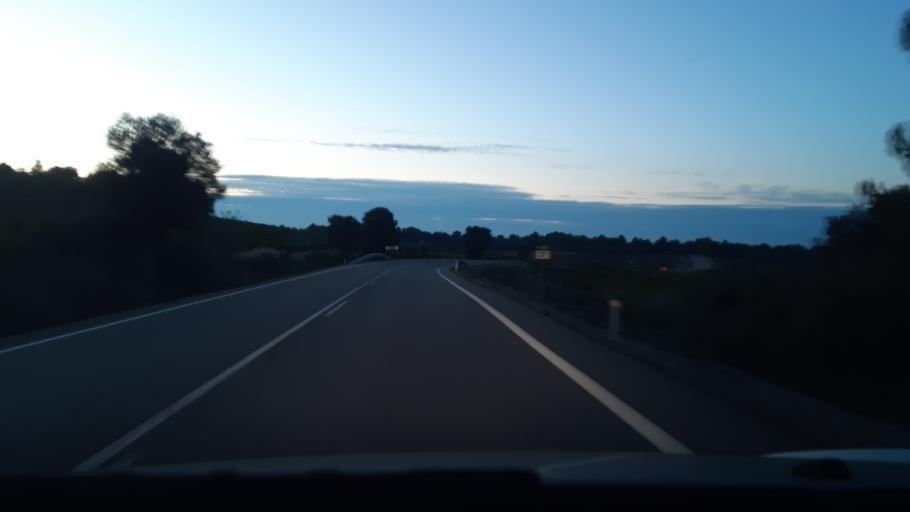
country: ES
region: Aragon
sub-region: Provincia de Teruel
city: Lledo
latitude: 40.9583
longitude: 0.2162
